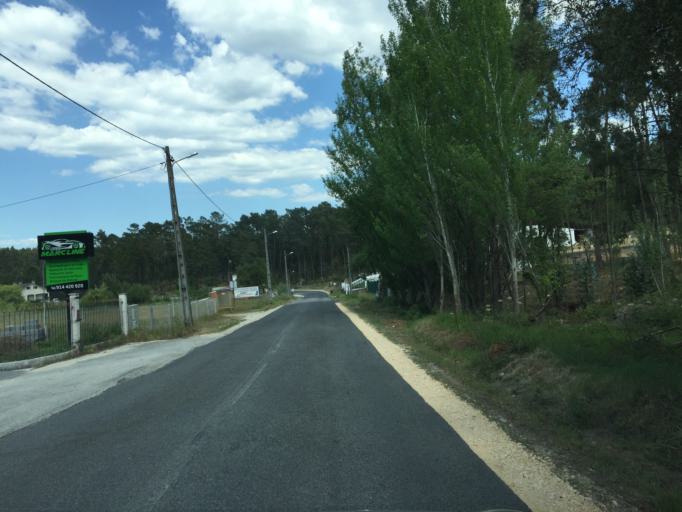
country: PT
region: Santarem
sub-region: Ourem
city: Ourem
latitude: 39.6937
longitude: -8.5409
